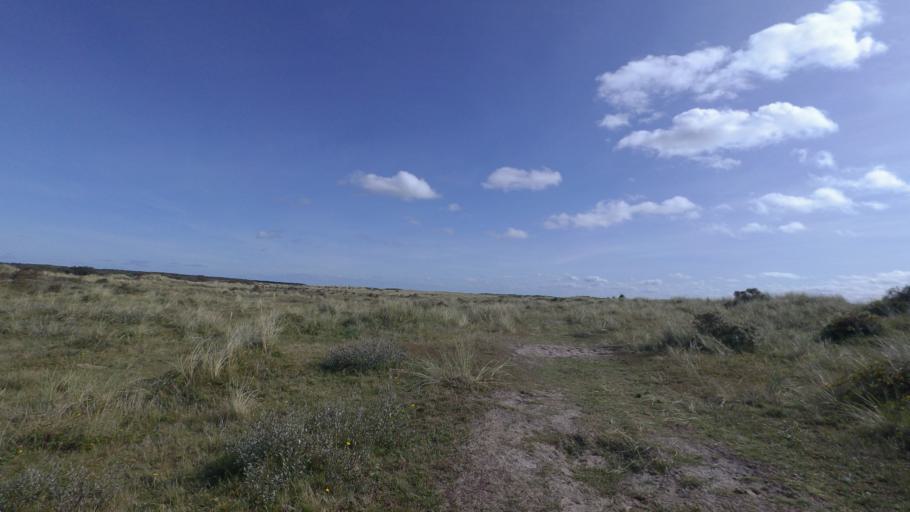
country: NL
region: Friesland
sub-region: Gemeente Ameland
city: Nes
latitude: 53.4507
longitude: 5.7328
